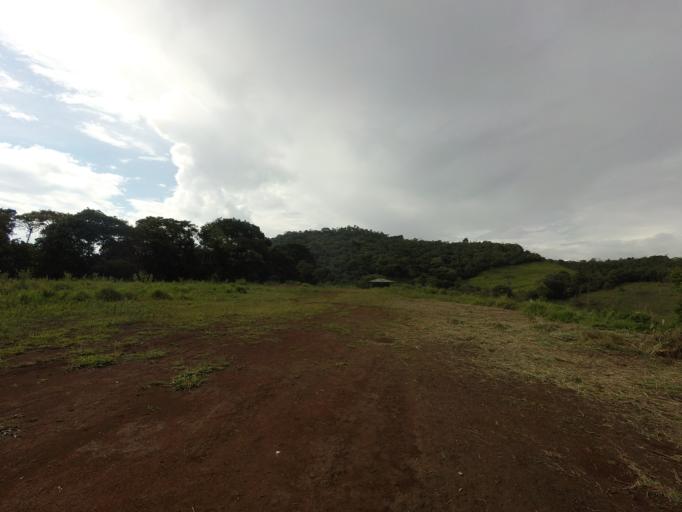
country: CO
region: Huila
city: San Agustin
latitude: 1.9120
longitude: -76.2929
